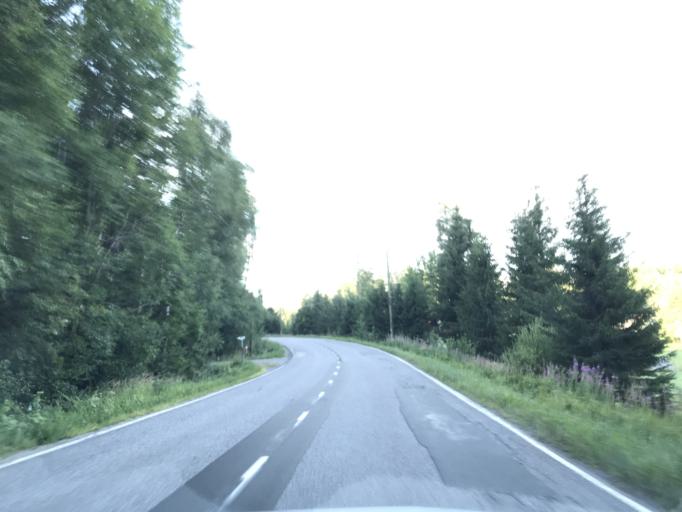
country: FI
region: Uusimaa
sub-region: Helsinki
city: Nurmijaervi
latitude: 60.3745
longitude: 24.6780
